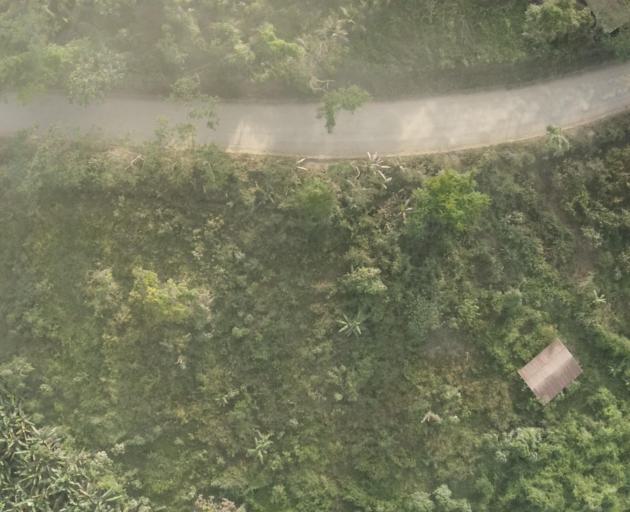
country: BO
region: La Paz
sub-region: Provincia Larecaja
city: Guanay
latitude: -15.7730
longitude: -67.6589
